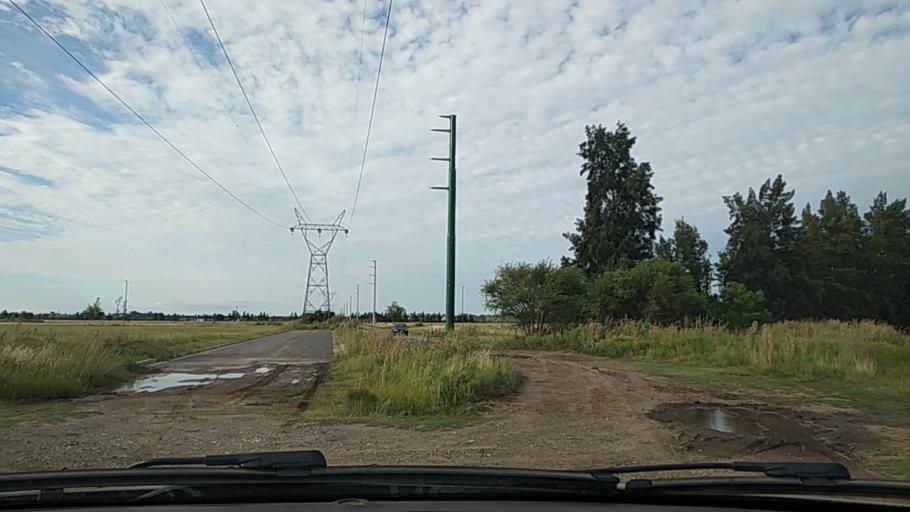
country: AR
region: Santa Fe
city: Perez
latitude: -32.9477
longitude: -60.7638
